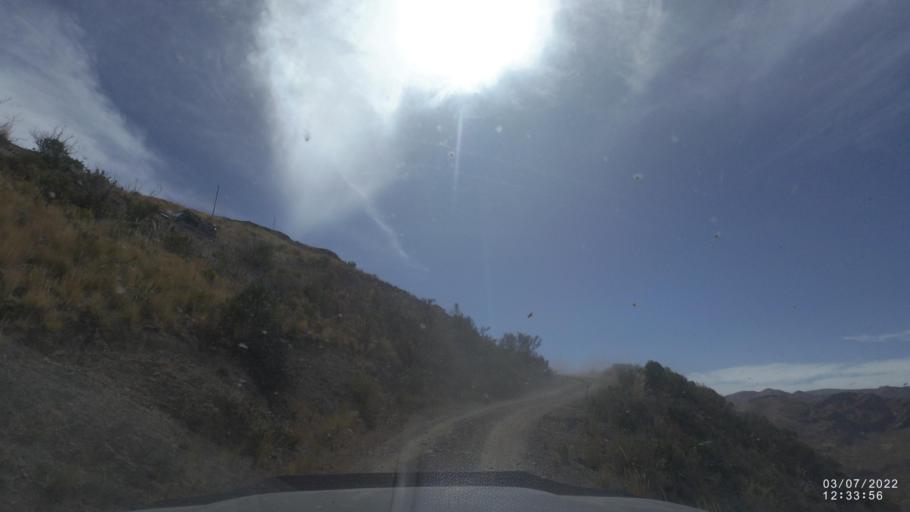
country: BO
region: Cochabamba
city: Irpa Irpa
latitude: -17.8070
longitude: -66.6058
